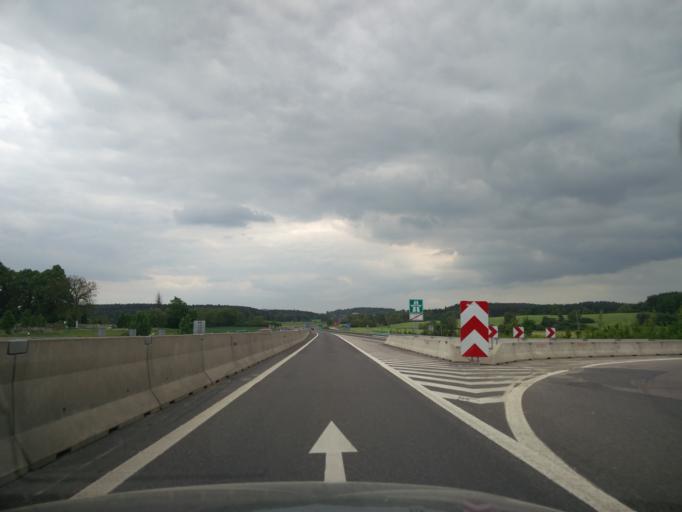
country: CZ
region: Jihocesky
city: Mirotice
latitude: 49.4133
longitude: 14.0376
